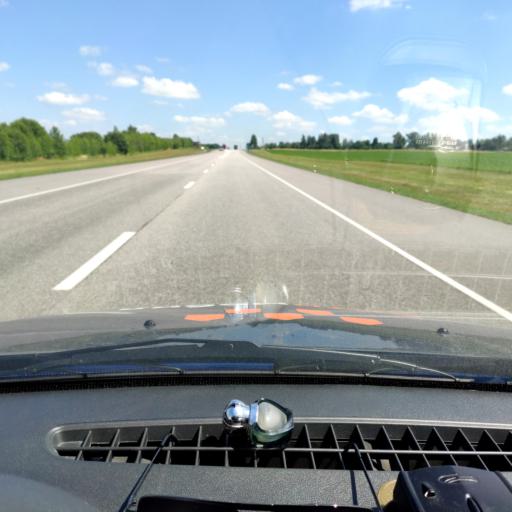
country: RU
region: Orjol
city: Orel
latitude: 52.8544
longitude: 36.2220
